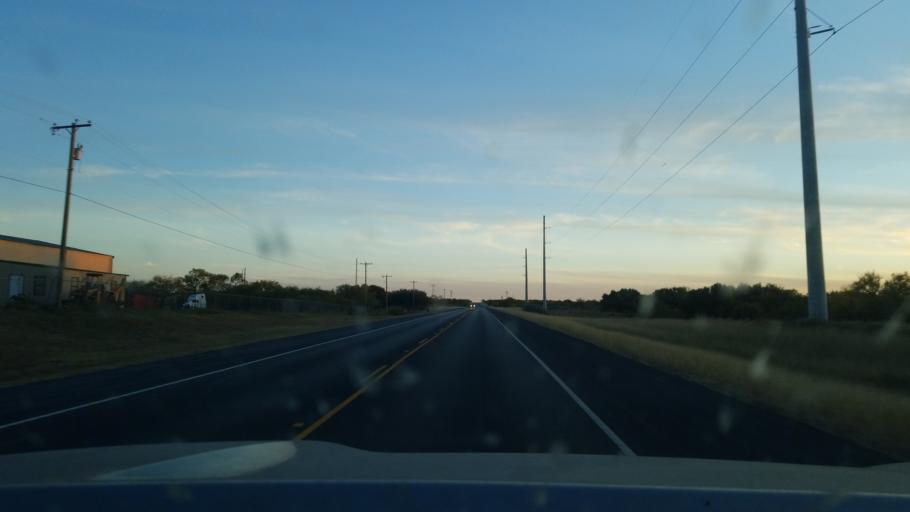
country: US
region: Texas
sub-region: Stephens County
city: Breckenridge
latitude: 32.6992
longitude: -98.9027
